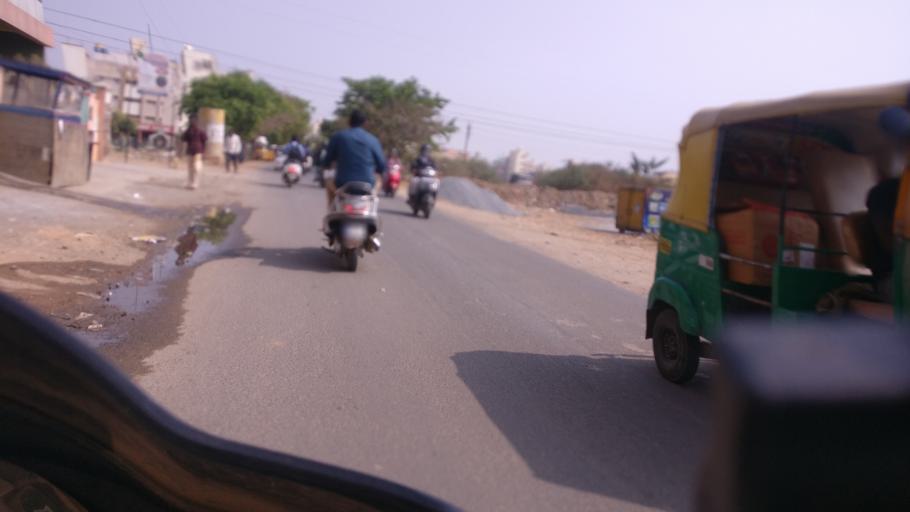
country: IN
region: Karnataka
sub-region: Bangalore Urban
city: Bangalore
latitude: 12.8744
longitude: 77.6543
